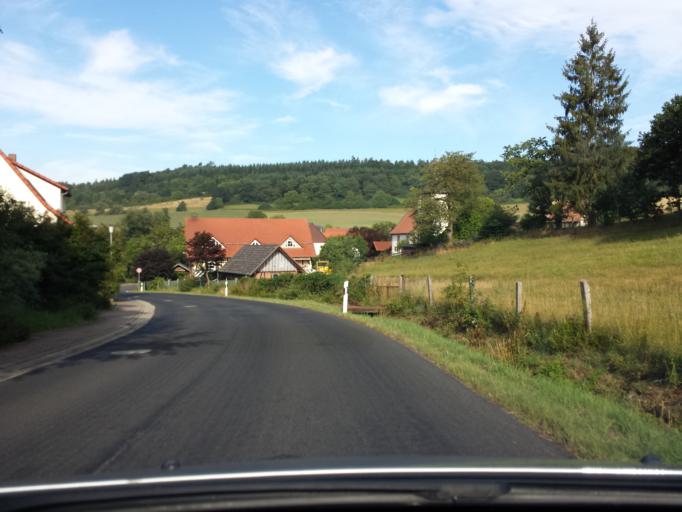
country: DE
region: Hesse
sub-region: Regierungsbezirk Kassel
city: Kirchheim
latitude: 50.8617
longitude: 9.6000
